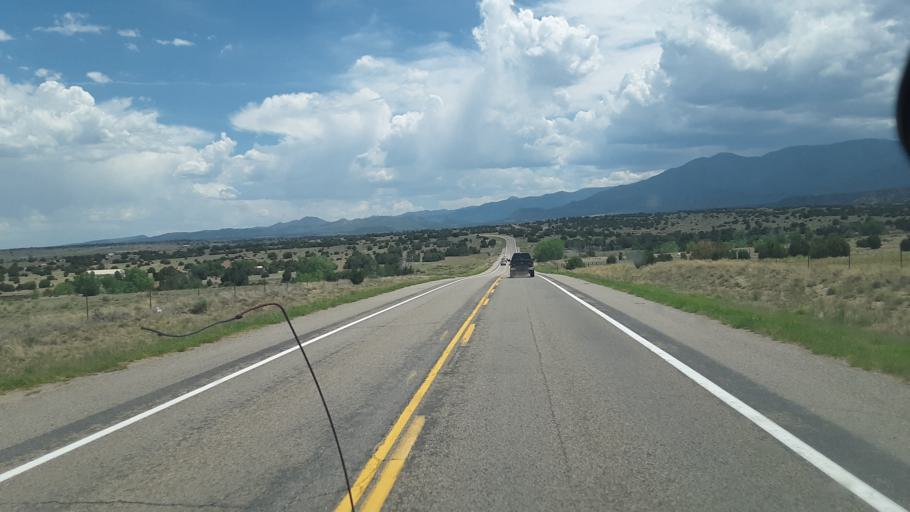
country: US
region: Colorado
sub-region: Fremont County
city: Florence
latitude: 38.3182
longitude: -105.1052
